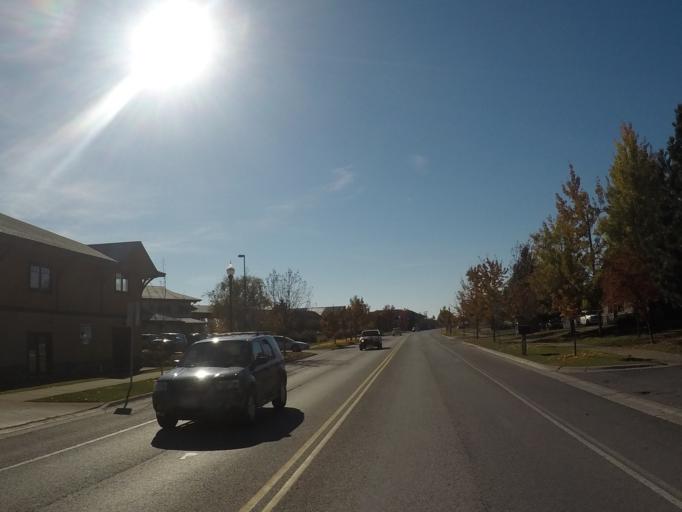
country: US
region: Montana
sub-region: Flathead County
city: Whitefish
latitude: 48.4019
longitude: -114.3379
